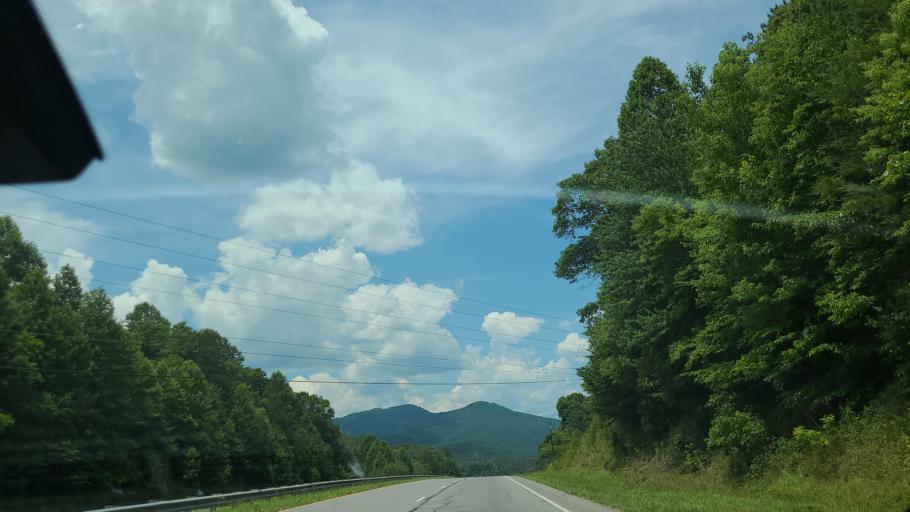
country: US
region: North Carolina
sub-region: Cherokee County
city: Murphy
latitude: 35.0223
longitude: -84.1980
